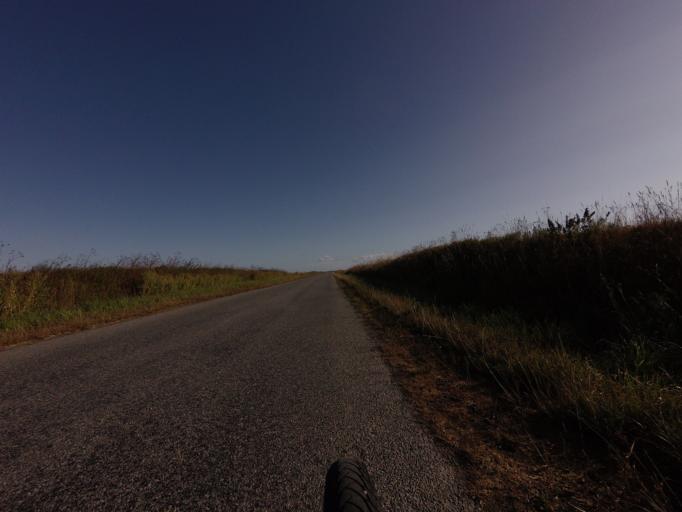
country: DK
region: North Denmark
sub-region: Hjorring Kommune
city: Vra
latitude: 57.3895
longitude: 9.9264
